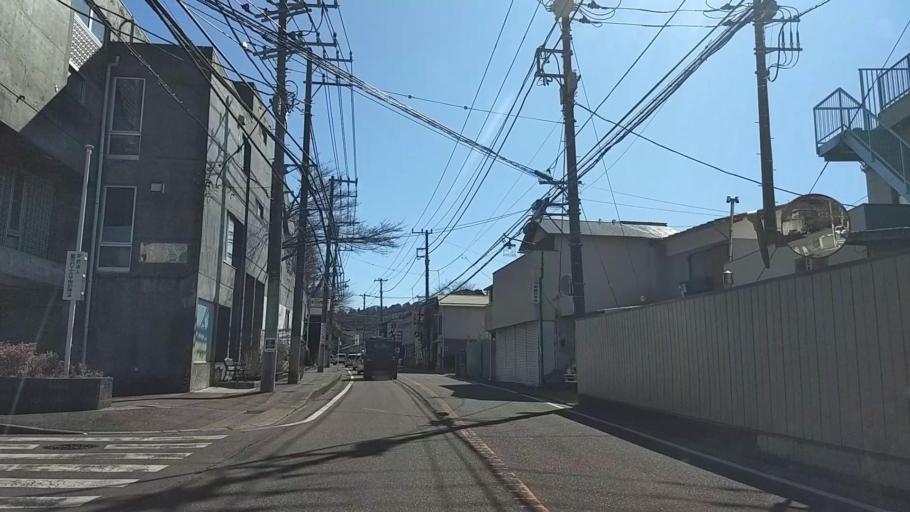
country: JP
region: Kanagawa
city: Kamakura
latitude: 35.3242
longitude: 139.5247
